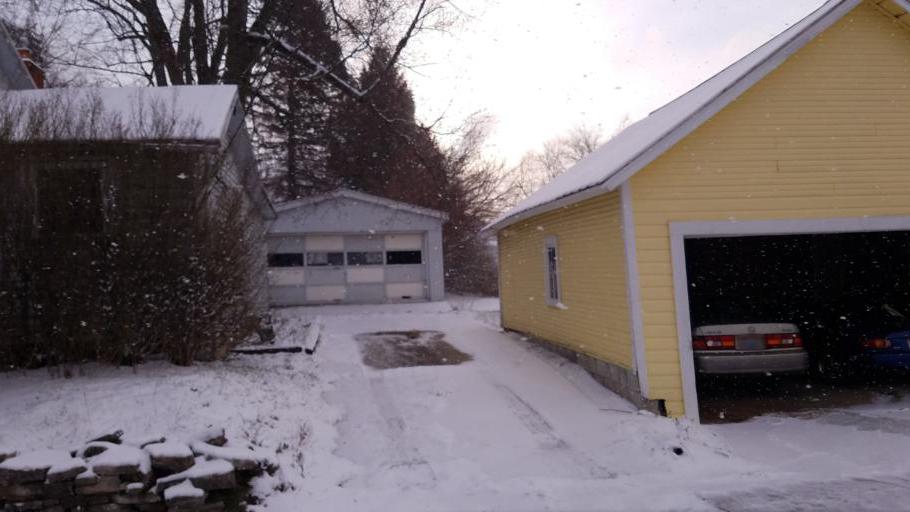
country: US
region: Ohio
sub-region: Knox County
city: Fredericktown
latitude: 40.4830
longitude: -82.5473
